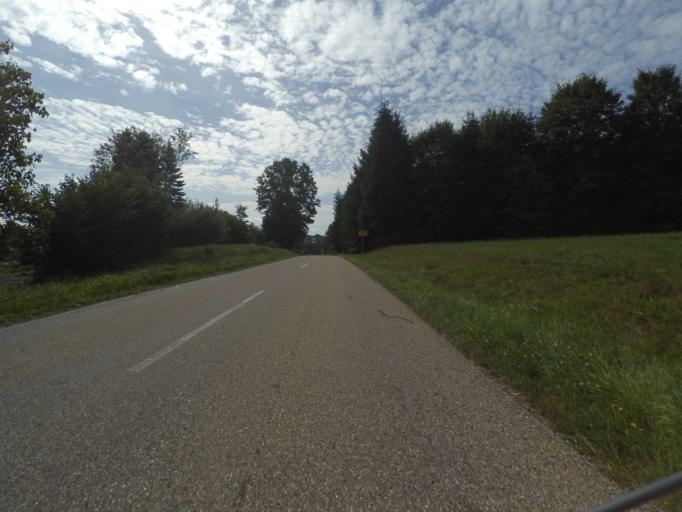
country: DE
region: Baden-Wuerttemberg
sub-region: Freiburg Region
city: Friedenweiler
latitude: 47.8960
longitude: 8.2934
